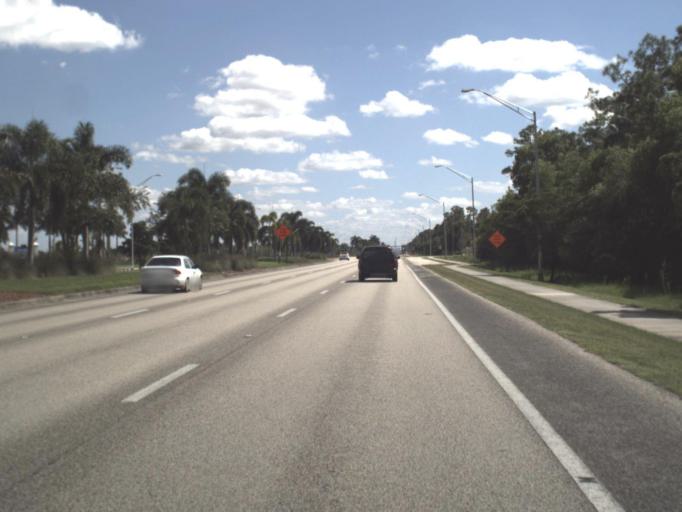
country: US
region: Florida
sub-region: Collier County
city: Lely Resort
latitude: 26.0700
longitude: -81.7099
